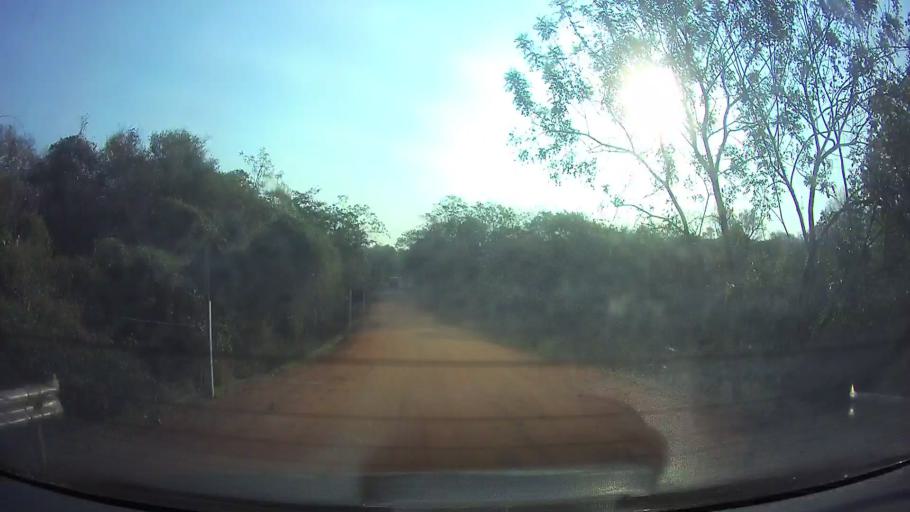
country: PY
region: Central
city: Limpio
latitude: -25.2173
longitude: -57.4951
